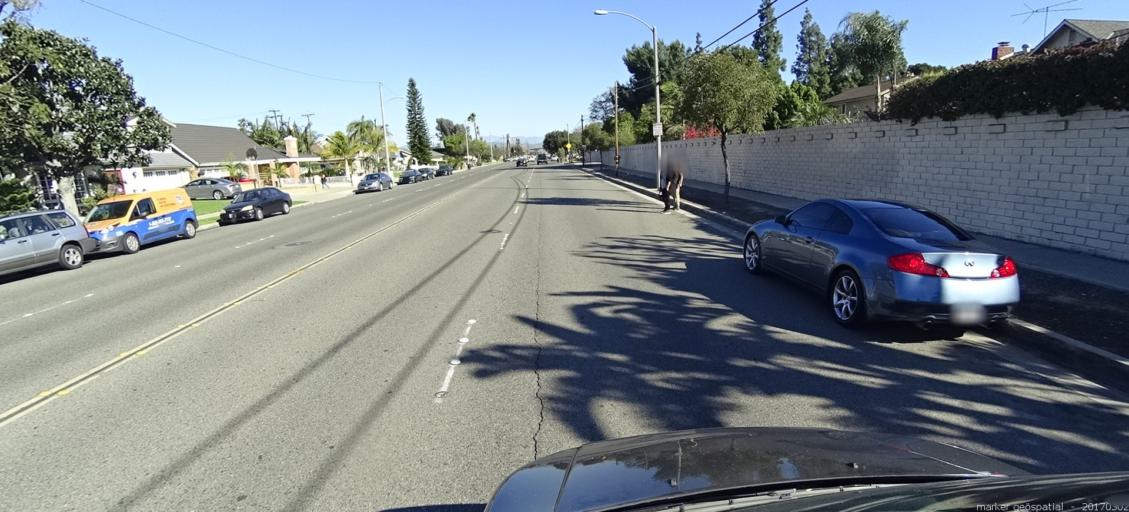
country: US
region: California
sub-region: Orange County
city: Placentia
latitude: 33.8408
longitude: -117.8804
